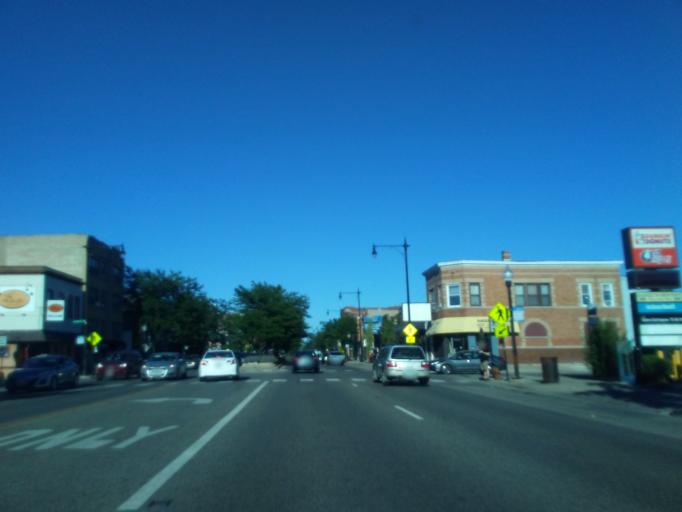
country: US
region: Illinois
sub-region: Cook County
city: Lincolnwood
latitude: 41.9539
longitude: -87.7060
